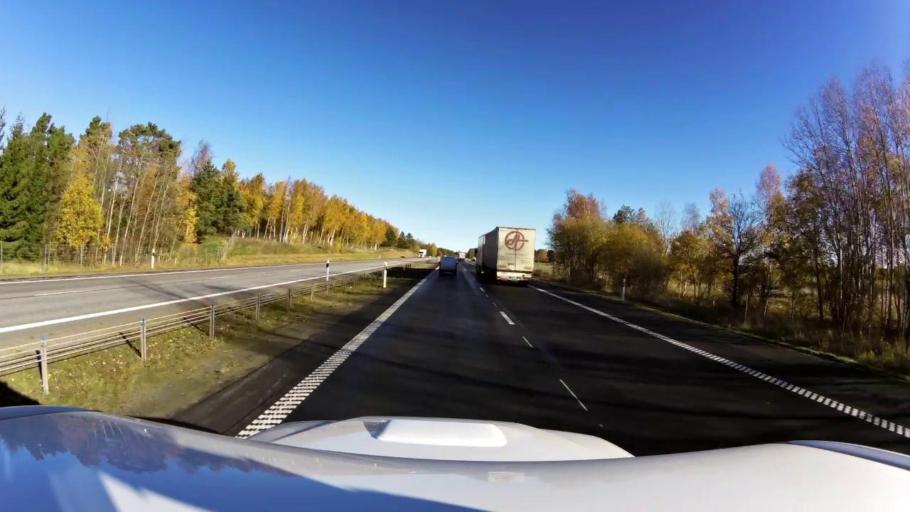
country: SE
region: OEstergoetland
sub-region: Linkopings Kommun
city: Vikingstad
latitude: 58.3964
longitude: 15.4262
